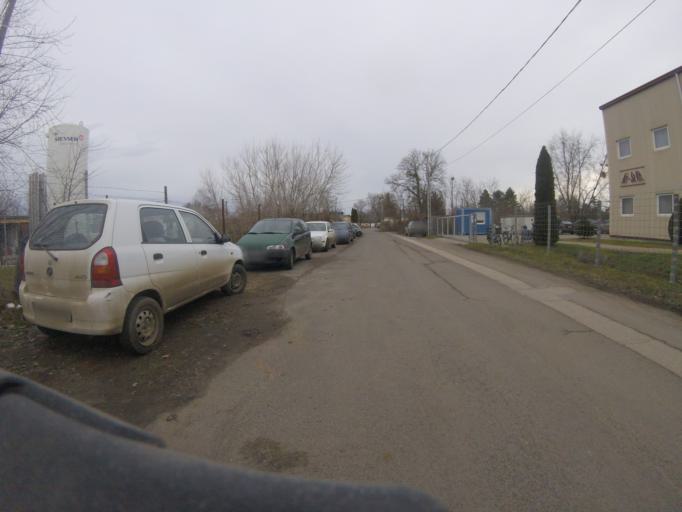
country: HU
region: Tolna
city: Dombovar
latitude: 46.3496
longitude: 18.1222
